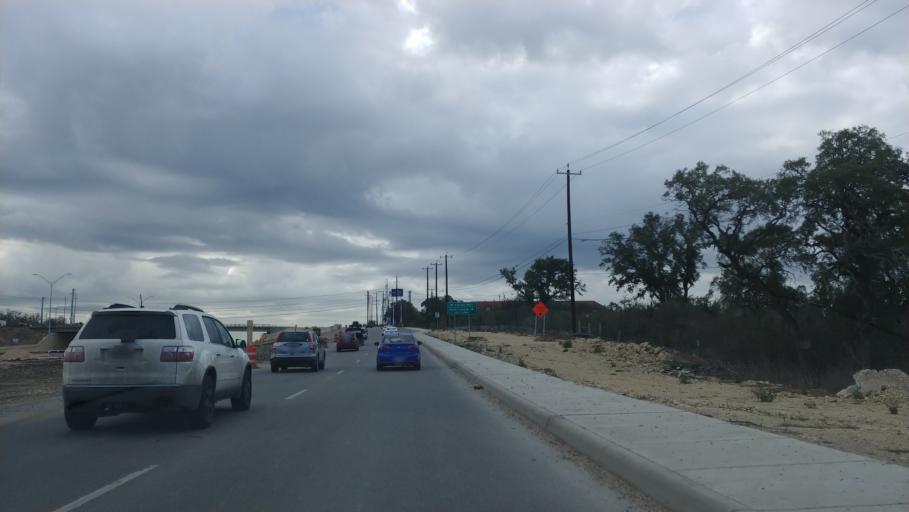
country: US
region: Texas
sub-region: Bexar County
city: Lackland Air Force Base
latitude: 29.4195
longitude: -98.7103
